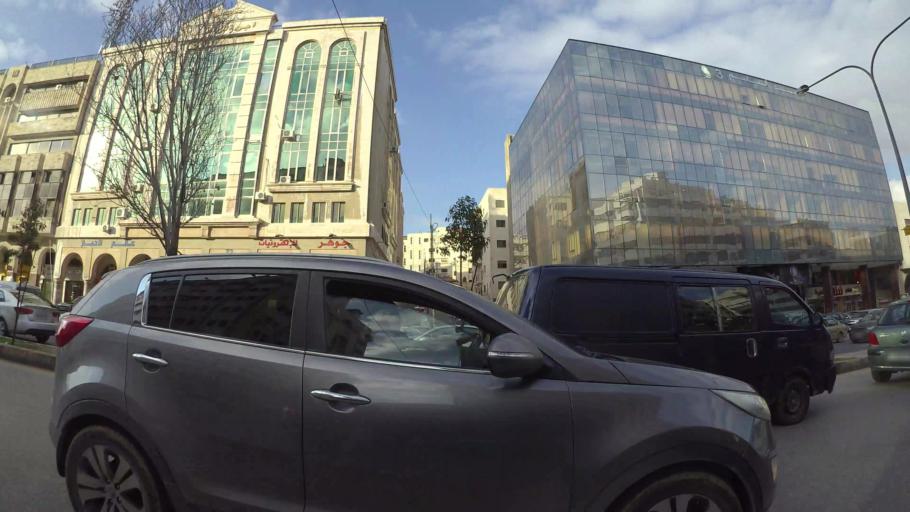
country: JO
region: Amman
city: Al Jubayhah
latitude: 31.9856
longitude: 35.8815
